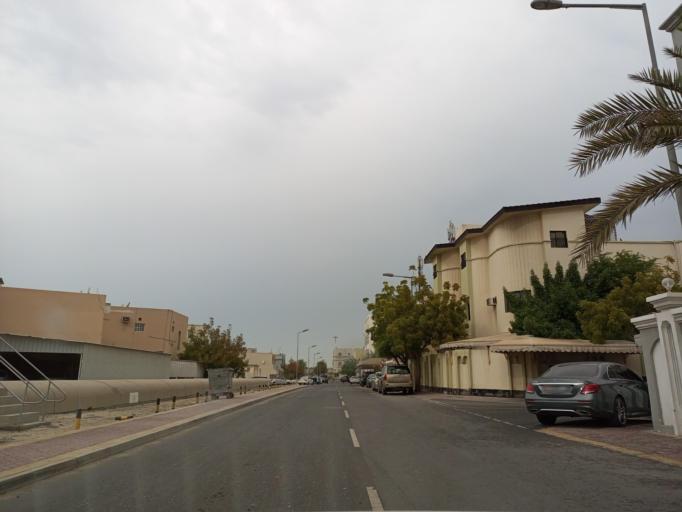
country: BH
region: Muharraq
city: Al Hadd
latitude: 26.2602
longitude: 50.6381
